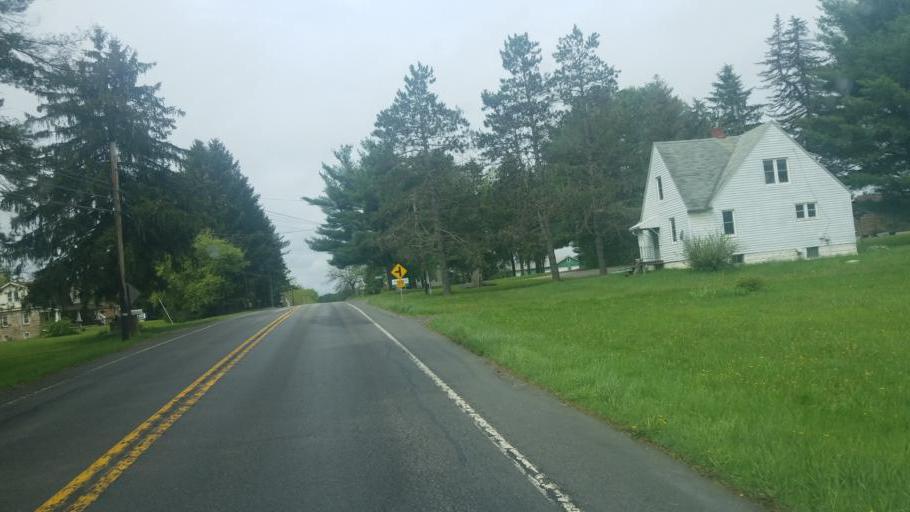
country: US
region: Pennsylvania
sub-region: Forest County
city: Marienville
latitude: 41.4558
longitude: -79.1521
